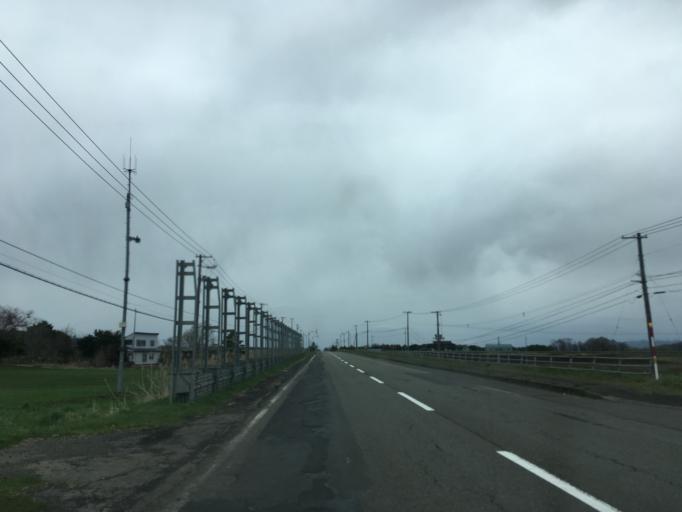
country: JP
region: Hokkaido
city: Chitose
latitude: 42.9255
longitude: 141.8080
